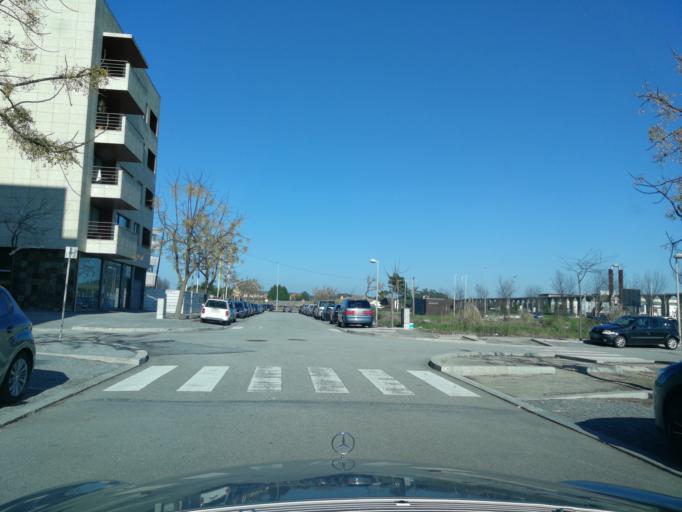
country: PT
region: Porto
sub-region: Vila do Conde
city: Vila do Conde
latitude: 41.3641
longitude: -8.7431
